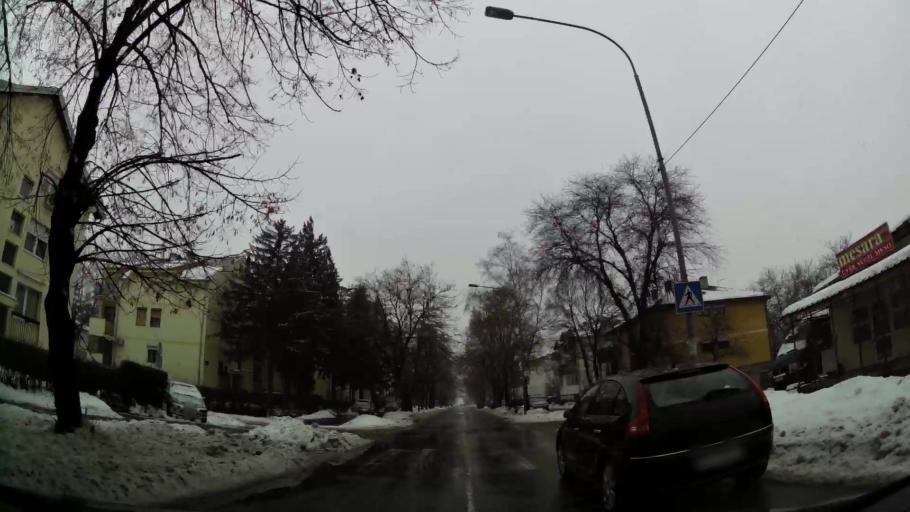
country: RS
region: Central Serbia
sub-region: Belgrade
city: Zemun
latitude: 44.8747
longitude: 20.3205
